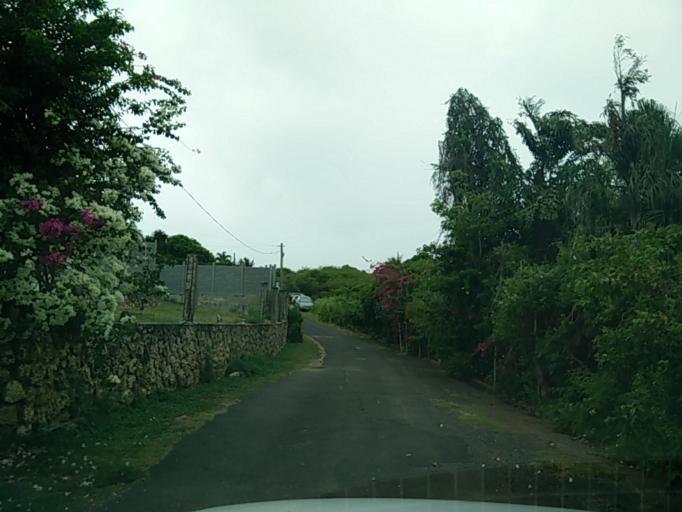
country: GP
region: Guadeloupe
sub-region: Guadeloupe
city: Sainte-Anne
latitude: 16.2105
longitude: -61.4226
